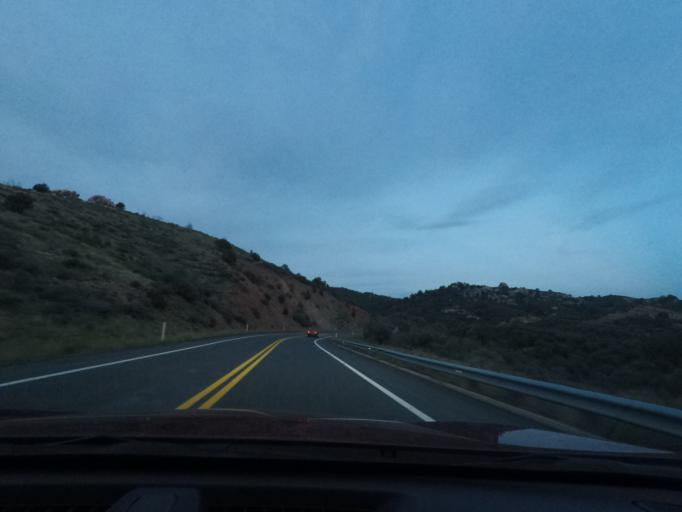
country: US
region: Arizona
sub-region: Yavapai County
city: Williamson
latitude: 34.5924
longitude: -112.5858
